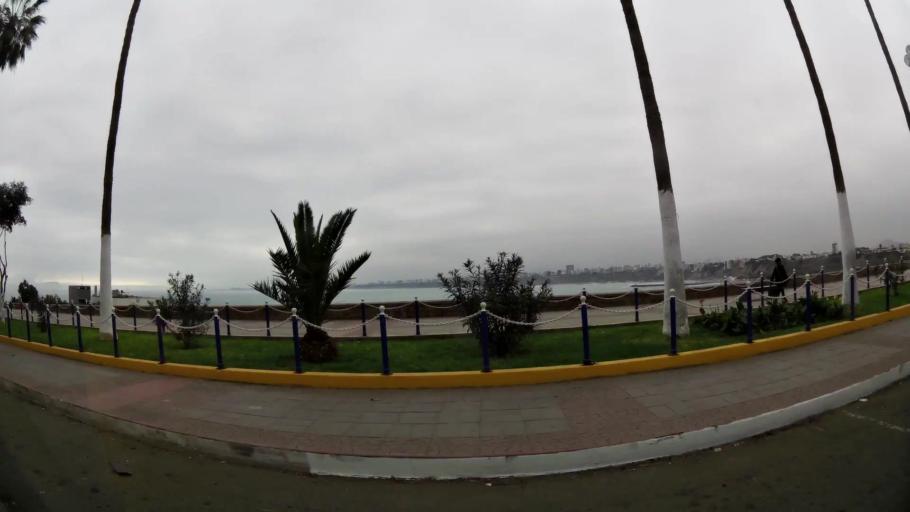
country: PE
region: Lima
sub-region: Lima
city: Surco
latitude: -12.1676
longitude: -77.0311
